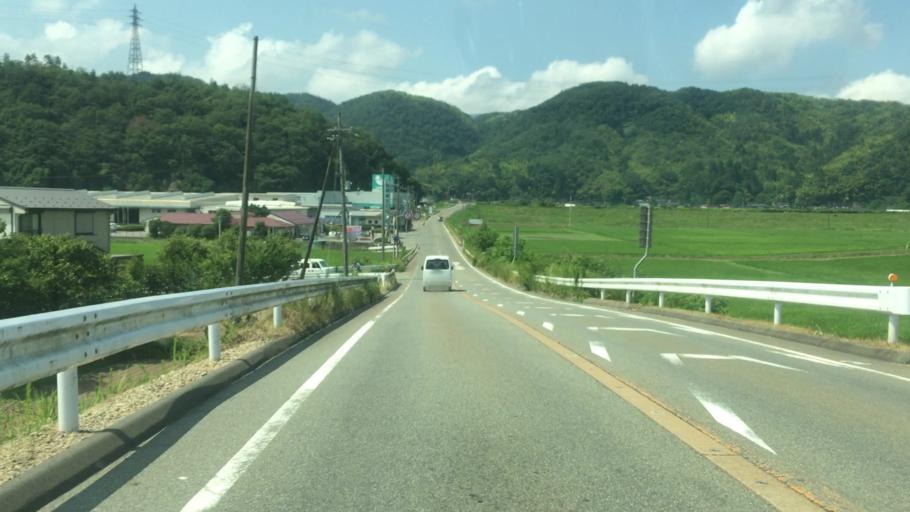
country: JP
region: Hyogo
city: Toyooka
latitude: 35.5591
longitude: 134.7965
